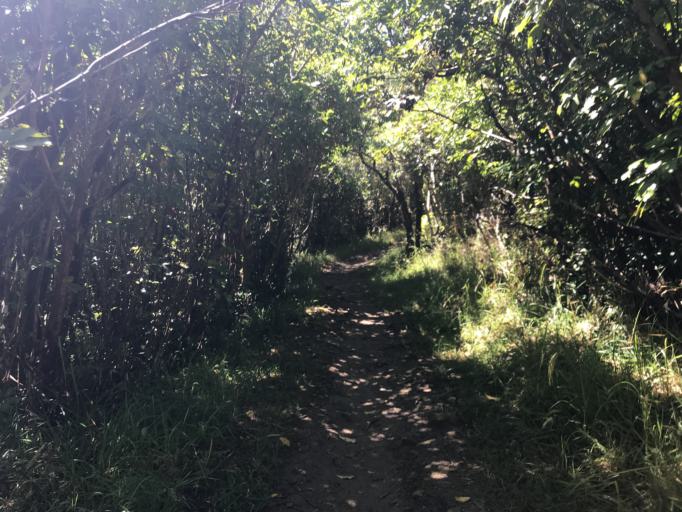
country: NZ
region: Marlborough
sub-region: Marlborough District
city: Picton
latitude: -41.2050
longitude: 174.0254
